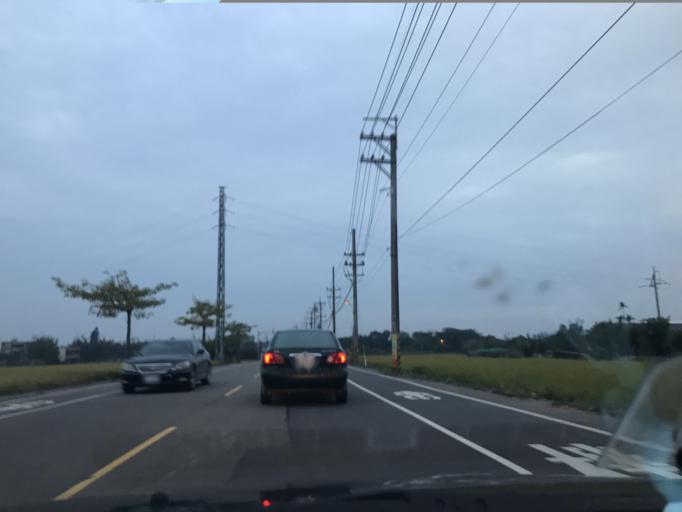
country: TW
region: Taiwan
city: Daxi
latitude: 24.9147
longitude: 121.2312
